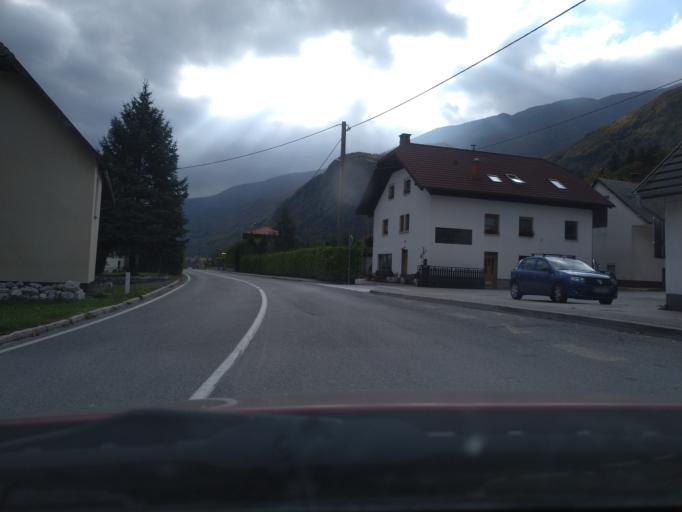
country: SI
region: Bovec
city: Bovec
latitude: 46.3042
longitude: 13.4815
